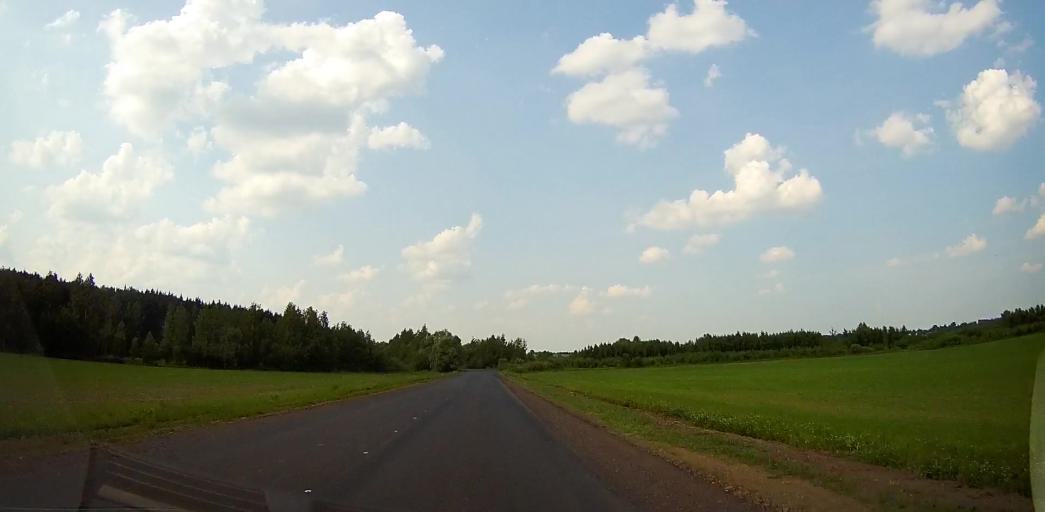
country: RU
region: Moskovskaya
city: Malino
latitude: 55.0606
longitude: 38.1363
